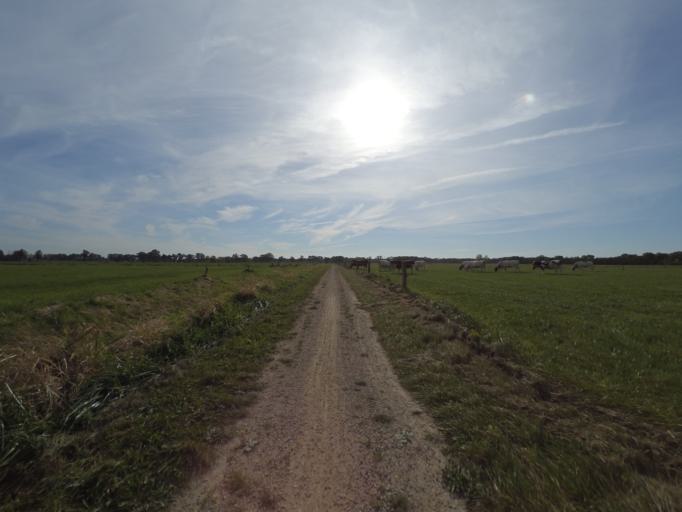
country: NL
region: Gelderland
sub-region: Gemeente Lochem
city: Laren
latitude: 52.2334
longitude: 6.3381
